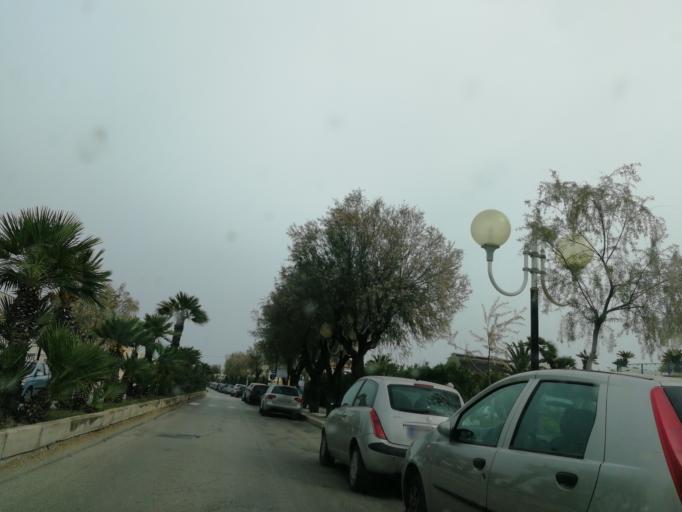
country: IT
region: Apulia
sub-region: Provincia di Barletta - Andria - Trani
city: Barletta
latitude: 41.3209
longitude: 16.2960
